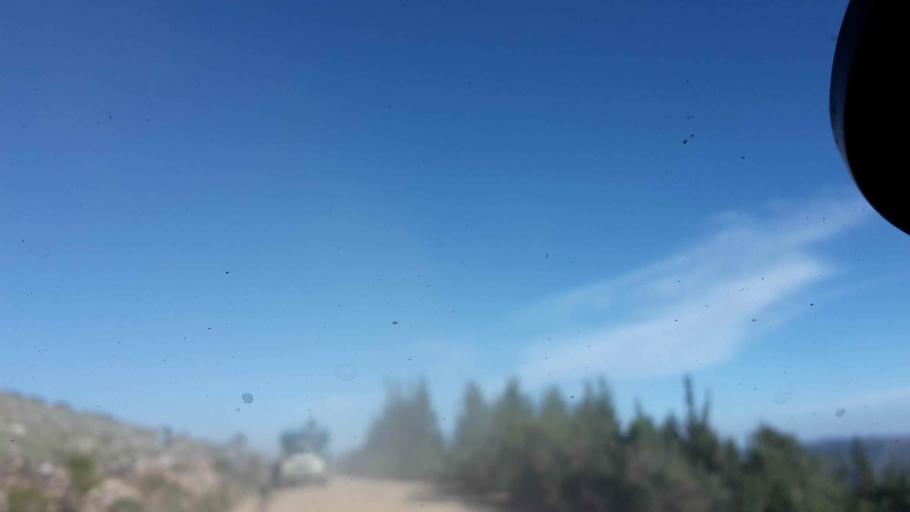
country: BO
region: Cochabamba
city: Arani
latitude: -17.7170
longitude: -65.6658
